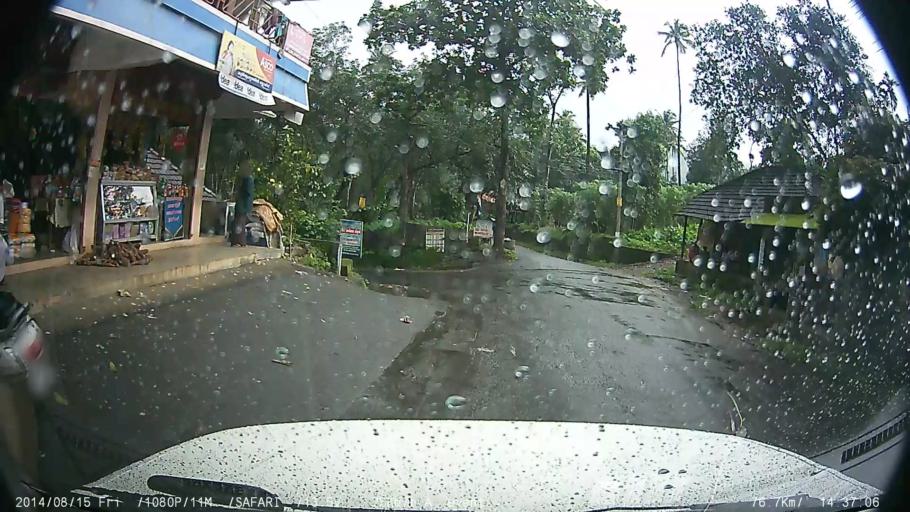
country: IN
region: Kerala
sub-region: Kottayam
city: Lalam
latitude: 9.8012
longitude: 76.7316
